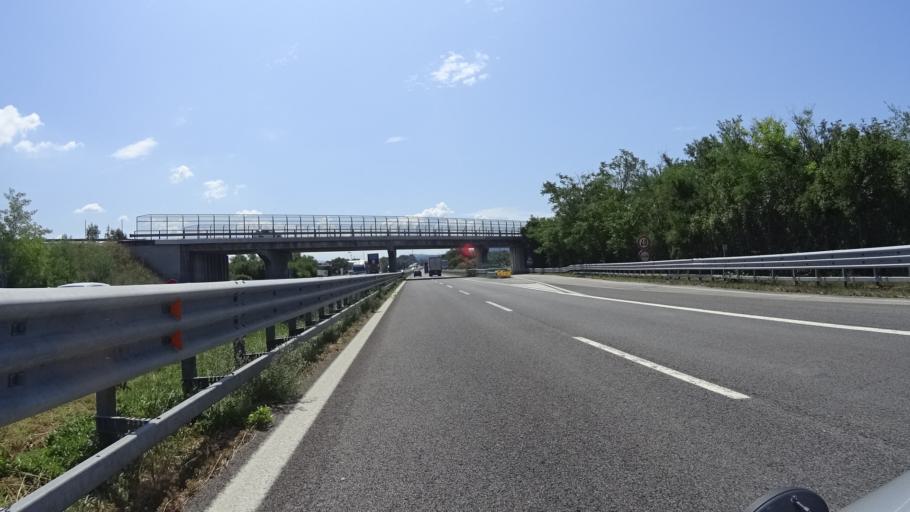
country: IT
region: Friuli Venezia Giulia
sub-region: Provincia di Trieste
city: Prosecco-Contovello
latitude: 45.7200
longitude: 13.7271
